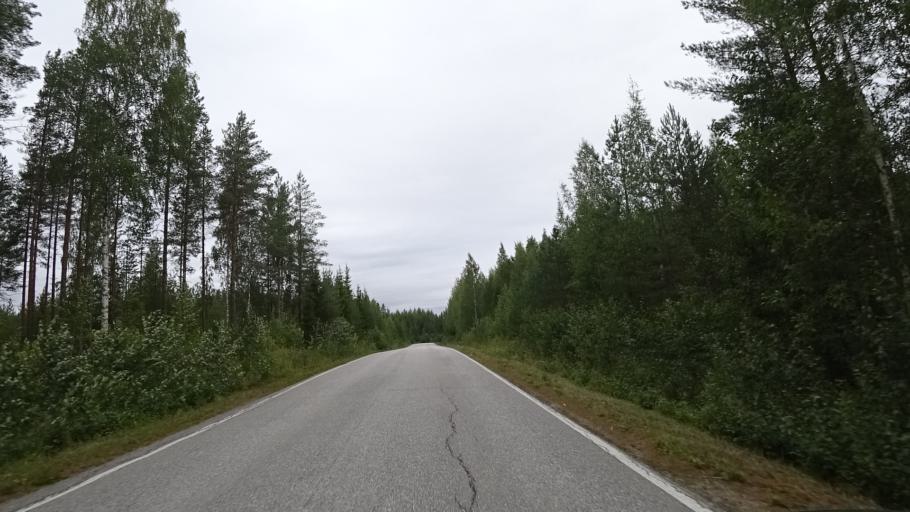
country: FI
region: North Karelia
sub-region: Pielisen Karjala
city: Lieksa
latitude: 63.3555
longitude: 30.2625
